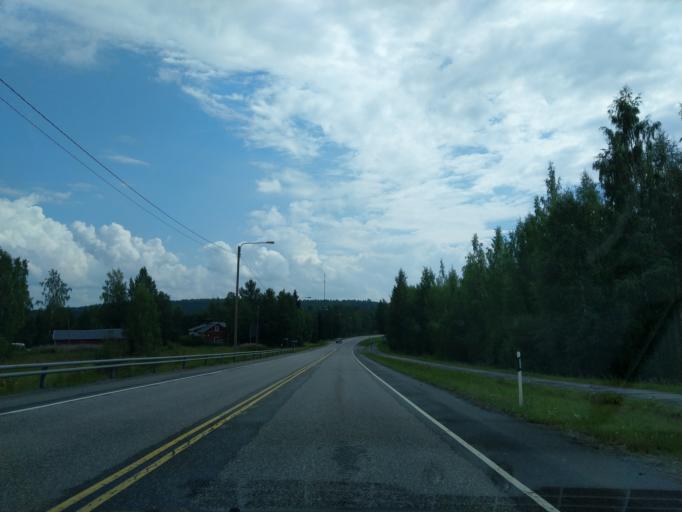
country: FI
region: South Karelia
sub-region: Imatra
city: Parikkala
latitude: 61.5783
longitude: 29.5022
